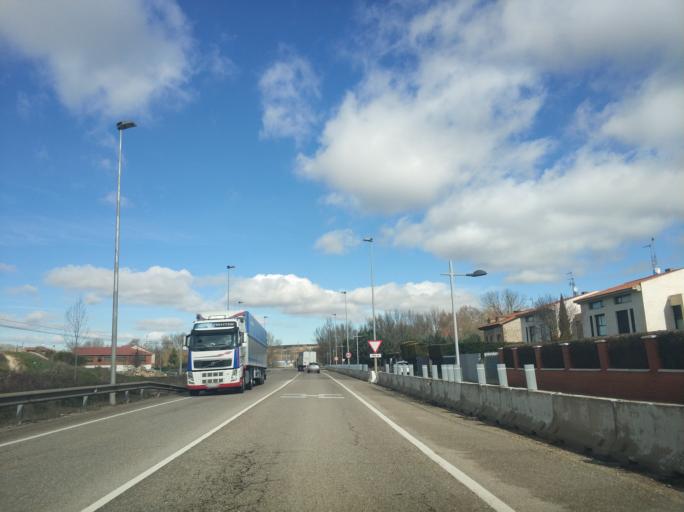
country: ES
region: Castille and Leon
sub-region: Provincia de Burgos
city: Saldana de Burgos
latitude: 42.2598
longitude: -3.6949
